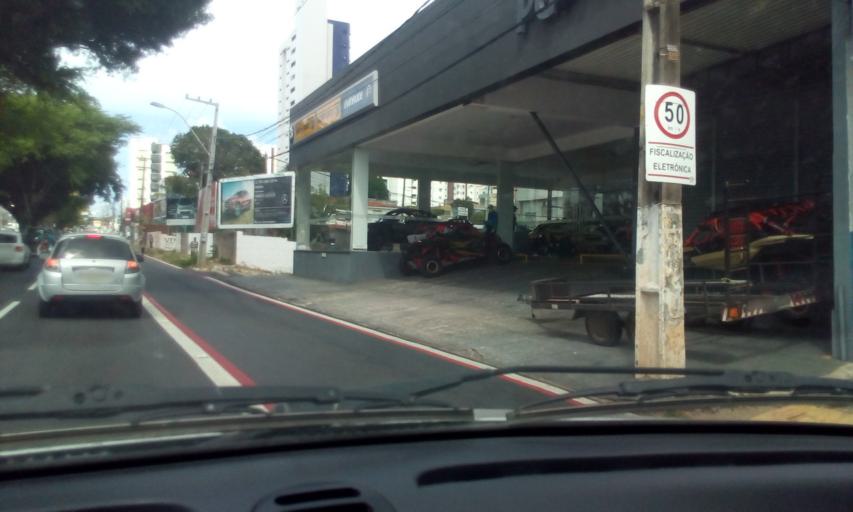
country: BR
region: Rio Grande do Norte
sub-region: Natal
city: Natal
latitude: -5.8042
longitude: -35.2073
